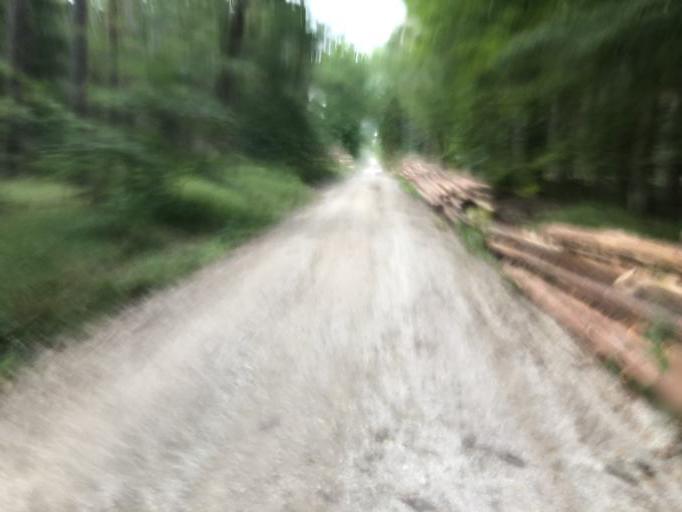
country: DE
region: Bavaria
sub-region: Regierungsbezirk Mittelfranken
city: Uttenreuth
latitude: 49.5760
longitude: 11.0766
